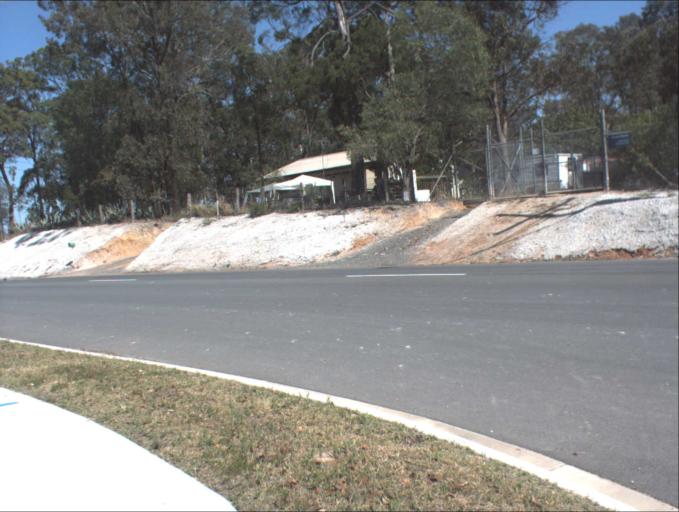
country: AU
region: Queensland
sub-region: Logan
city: Woodridge
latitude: -27.6553
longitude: 153.0804
